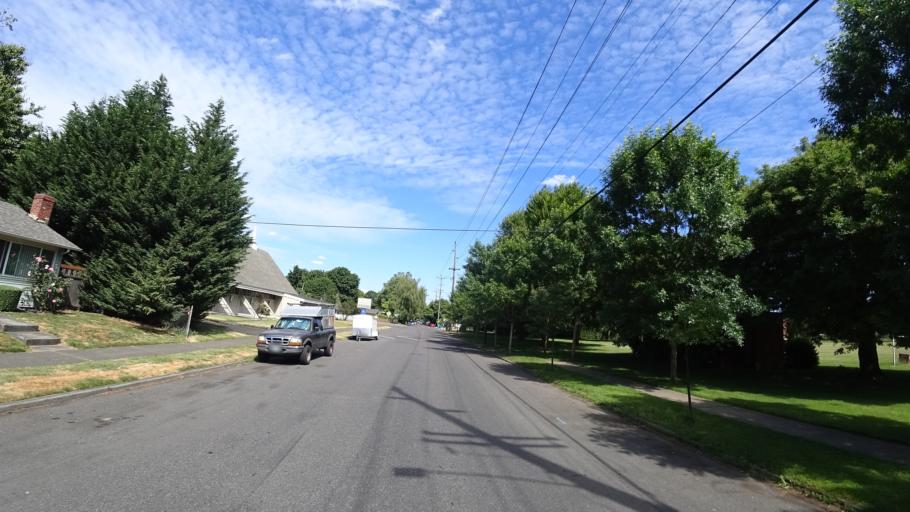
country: US
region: Washington
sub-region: Clark County
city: Vancouver
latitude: 45.5877
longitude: -122.7090
